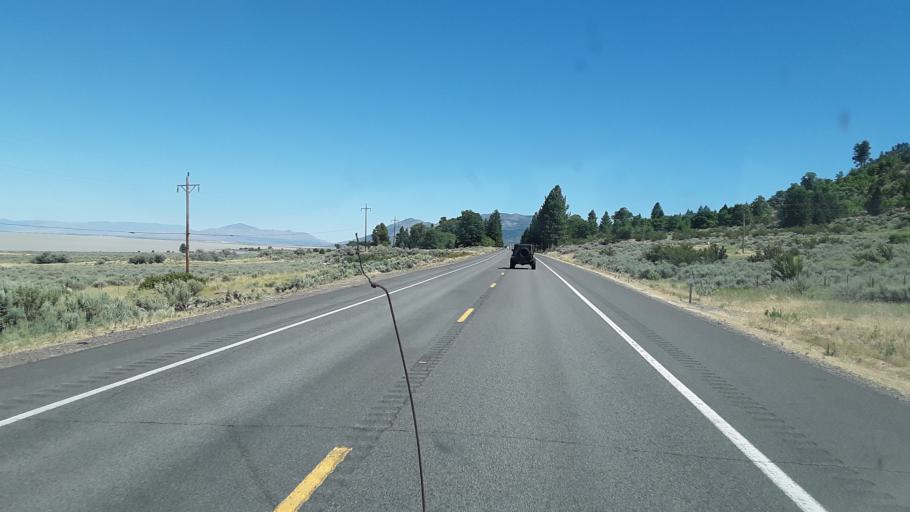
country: US
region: California
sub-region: Lassen County
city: Janesville
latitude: 40.2255
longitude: -120.4373
